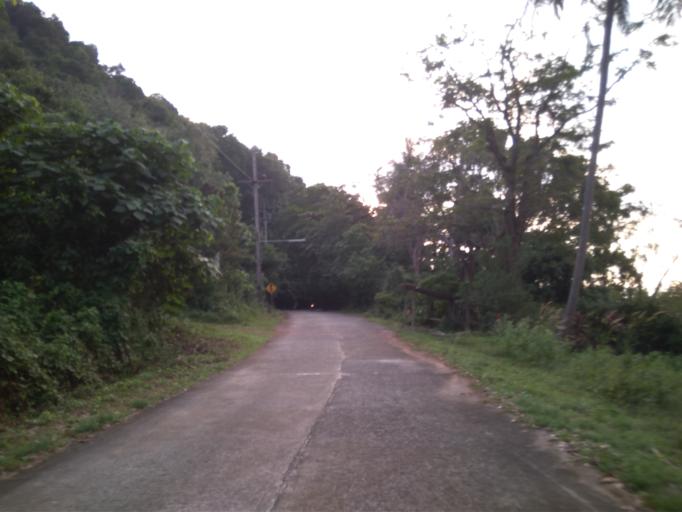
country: TH
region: Phangnga
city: Ko Yao
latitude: 8.1574
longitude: 98.6062
